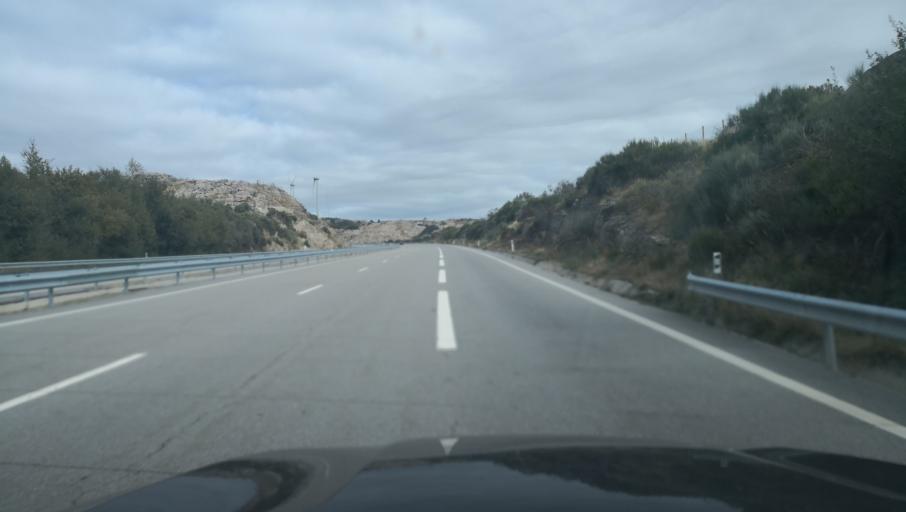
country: PT
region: Vila Real
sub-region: Vila Pouca de Aguiar
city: Vila Pouca de Aguiar
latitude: 41.4019
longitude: -7.6465
